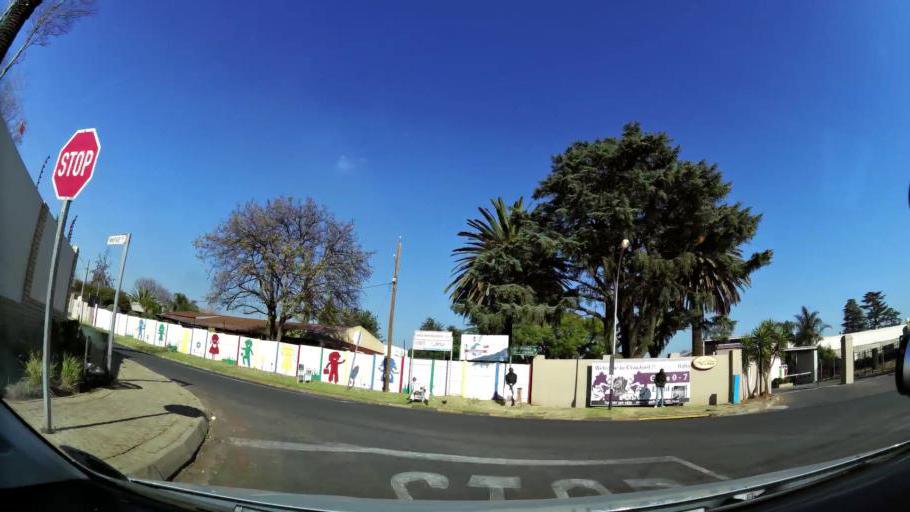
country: ZA
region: Gauteng
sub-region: Ekurhuleni Metropolitan Municipality
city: Germiston
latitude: -26.1642
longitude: 28.1440
